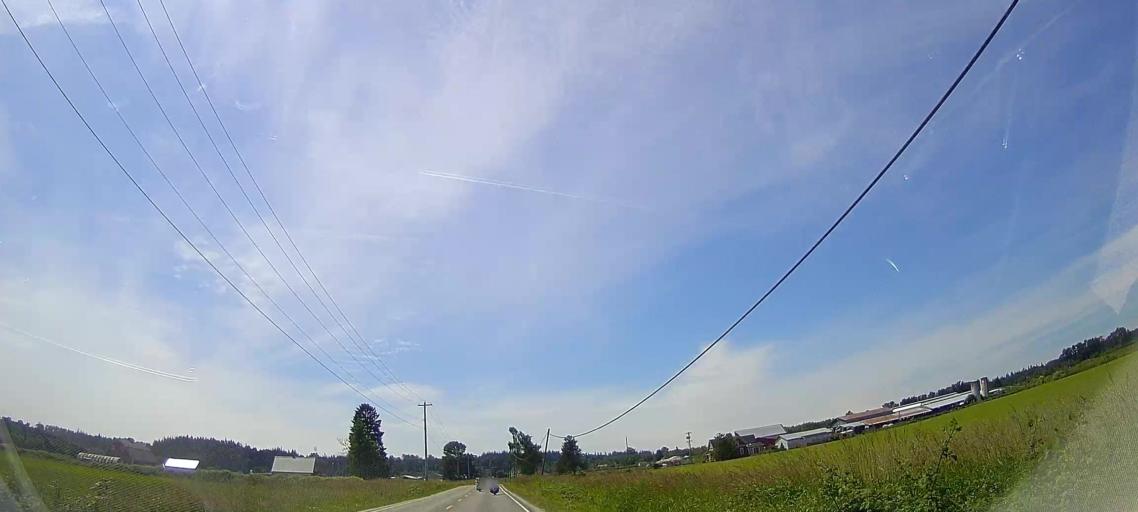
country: US
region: Washington
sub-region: Snohomish County
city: Smokey Point
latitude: 48.1880
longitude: -122.2144
